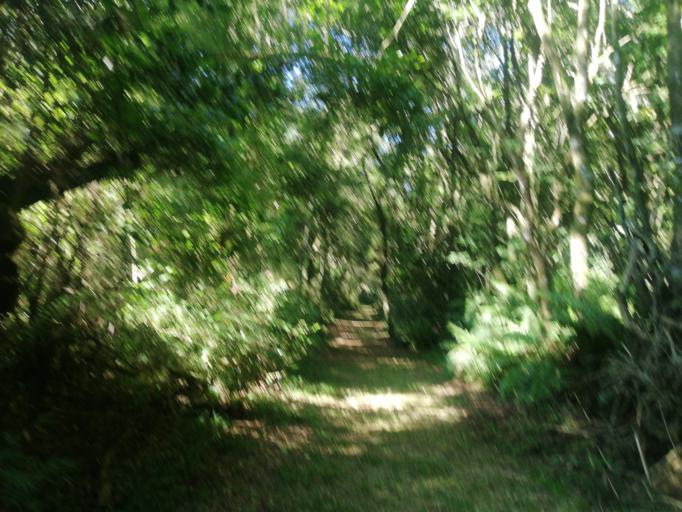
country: AR
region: Misiones
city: Cerro Azul
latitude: -27.7521
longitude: -55.5608
